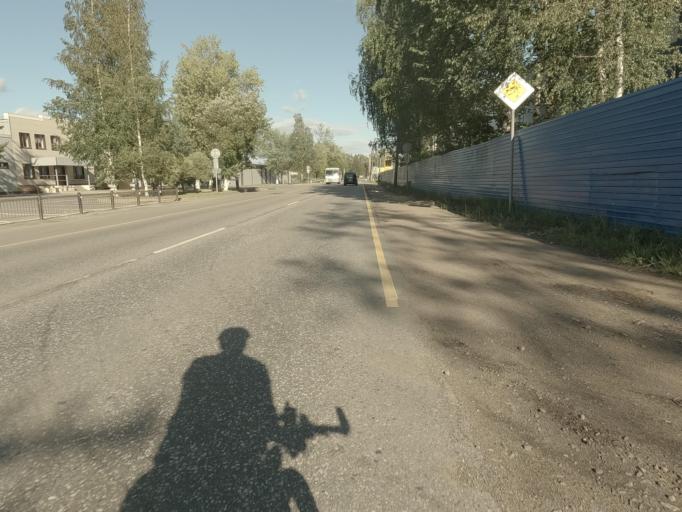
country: RU
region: Leningrad
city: Imeni Morozova
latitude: 59.9735
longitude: 31.0143
